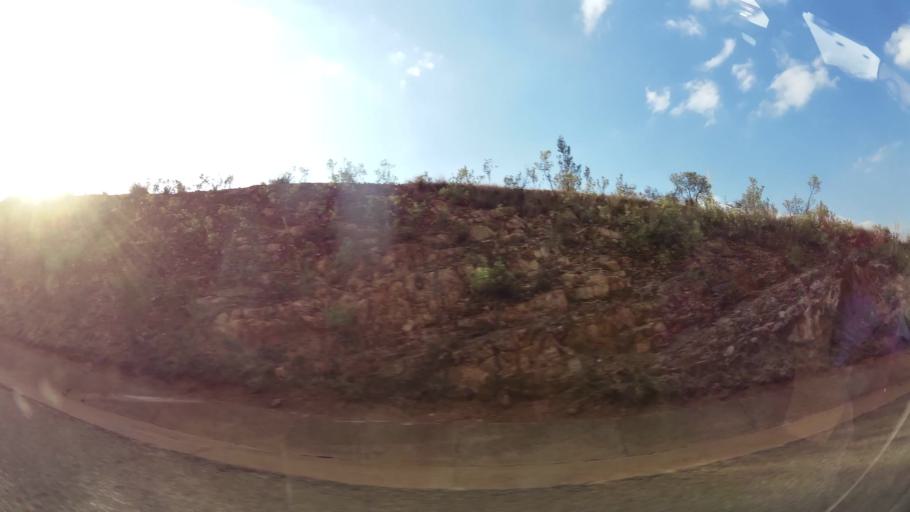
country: ZA
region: Gauteng
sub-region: West Rand District Municipality
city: Krugersdorp
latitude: -26.0848
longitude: 27.7447
